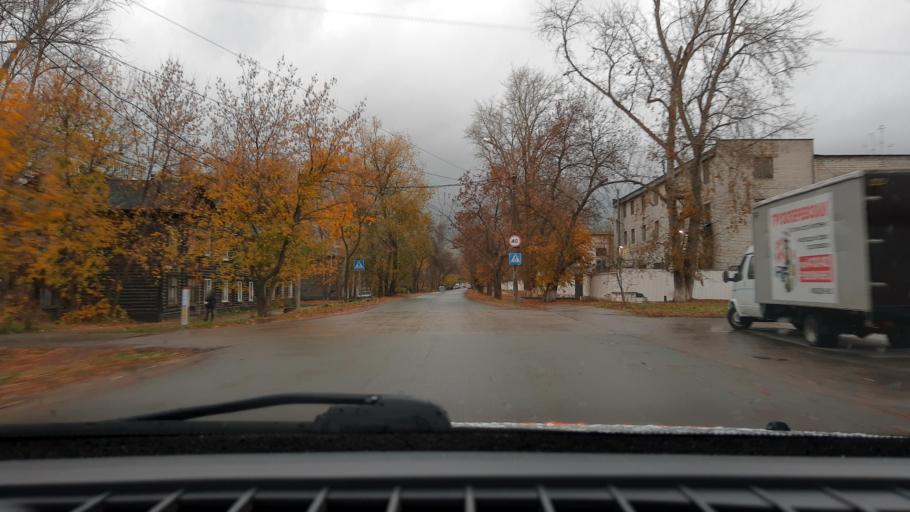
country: RU
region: Nizjnij Novgorod
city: Nizhniy Novgorod
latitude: 56.3095
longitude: 43.8907
